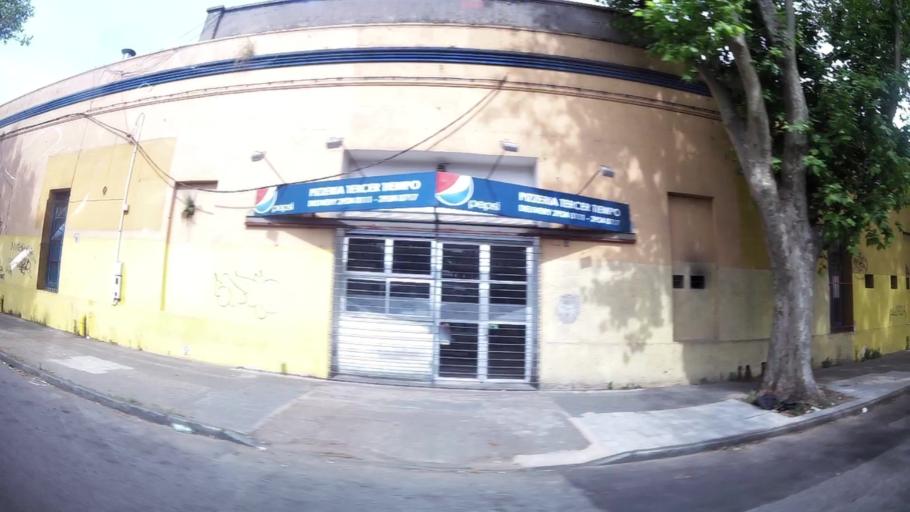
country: UY
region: Montevideo
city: Montevideo
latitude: -34.8891
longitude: -56.1943
